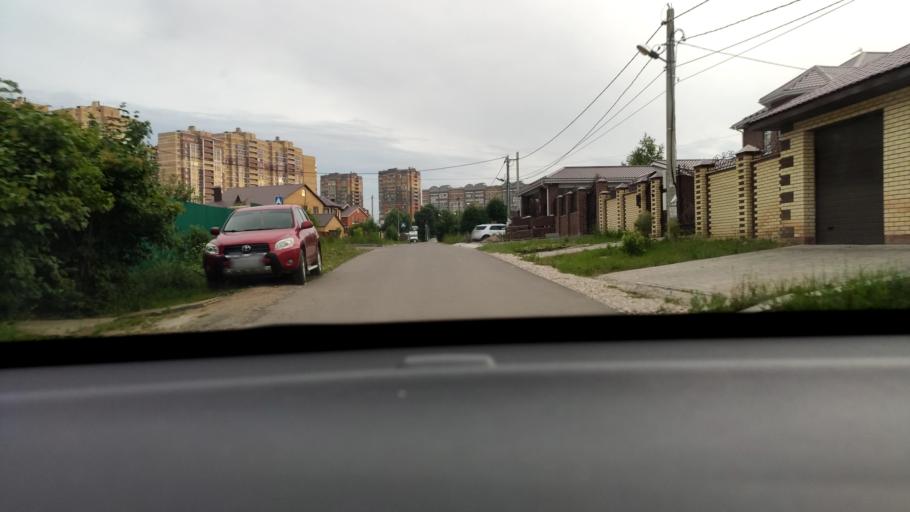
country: RU
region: Tatarstan
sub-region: Gorod Kazan'
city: Kazan
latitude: 55.7833
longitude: 49.2443
